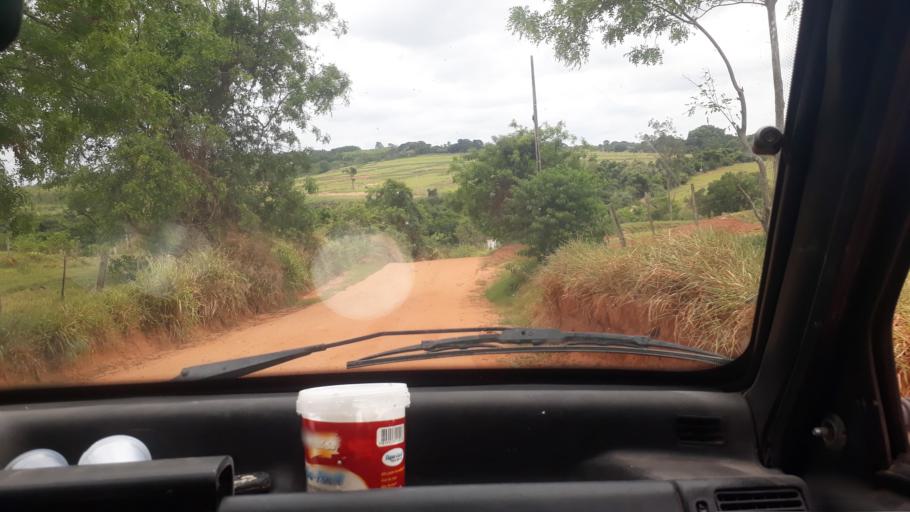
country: BR
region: Sao Paulo
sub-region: Regente Feijo
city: Regente Feijo
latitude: -22.2445
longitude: -51.2983
